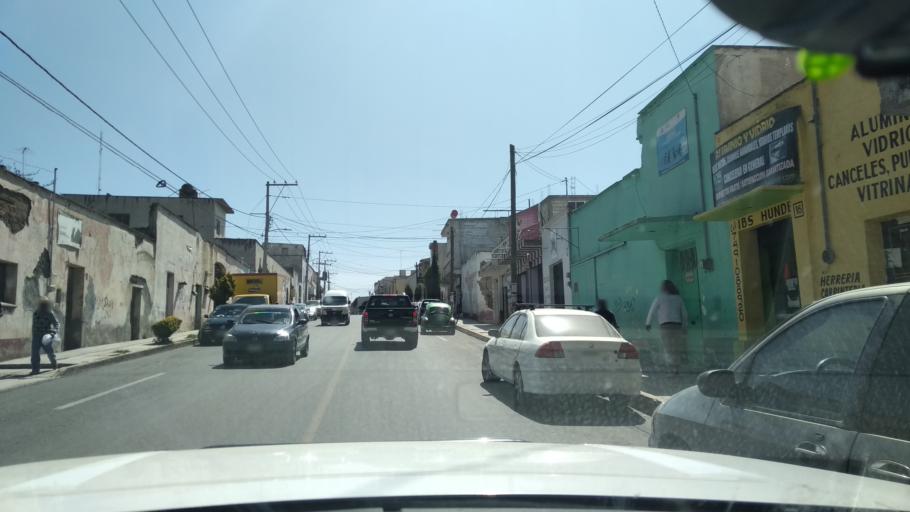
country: MX
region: Hidalgo
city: Calpulalpan
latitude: 19.5888
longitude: -98.5726
